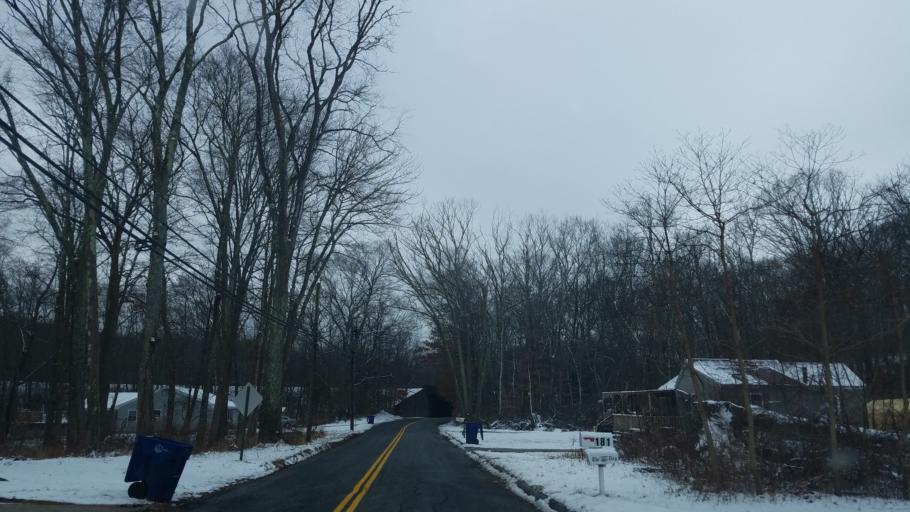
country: US
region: Connecticut
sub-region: New London County
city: Central Waterford
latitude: 41.3924
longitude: -72.1771
